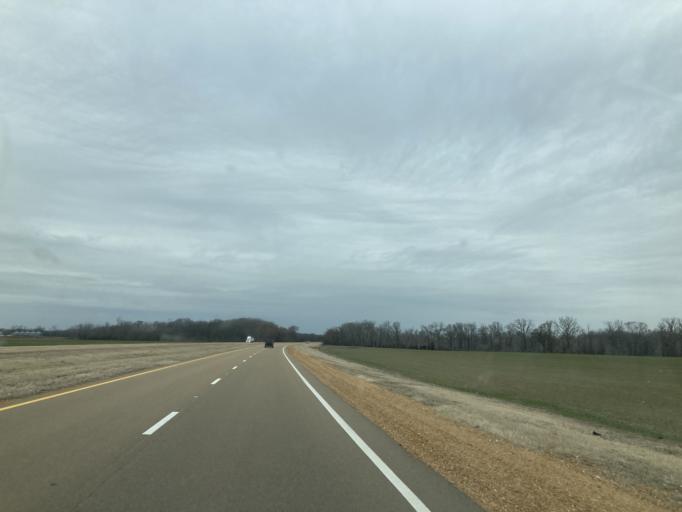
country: US
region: Mississippi
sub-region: Yazoo County
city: Yazoo City
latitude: 32.9839
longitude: -90.4632
